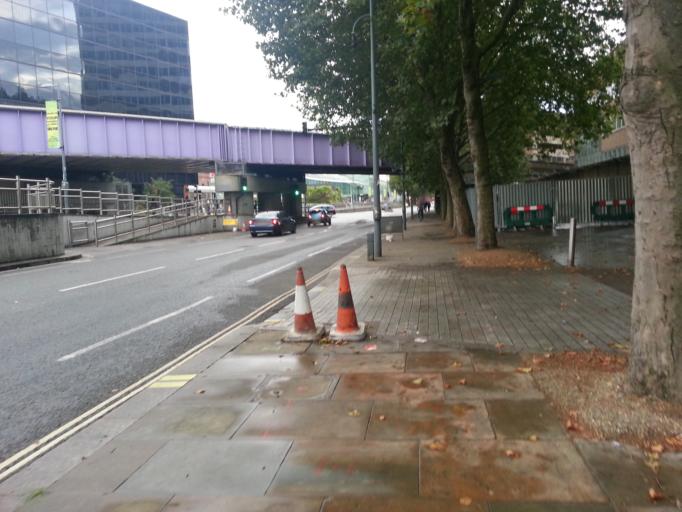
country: GB
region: England
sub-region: Greater London
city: Hammersmith
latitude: 51.5101
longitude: -0.2246
